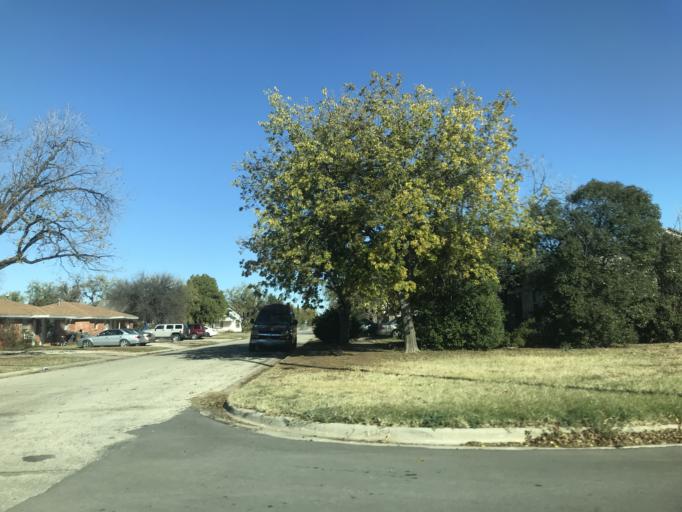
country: US
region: Texas
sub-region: Taylor County
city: Abilene
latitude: 32.4580
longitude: -99.7478
